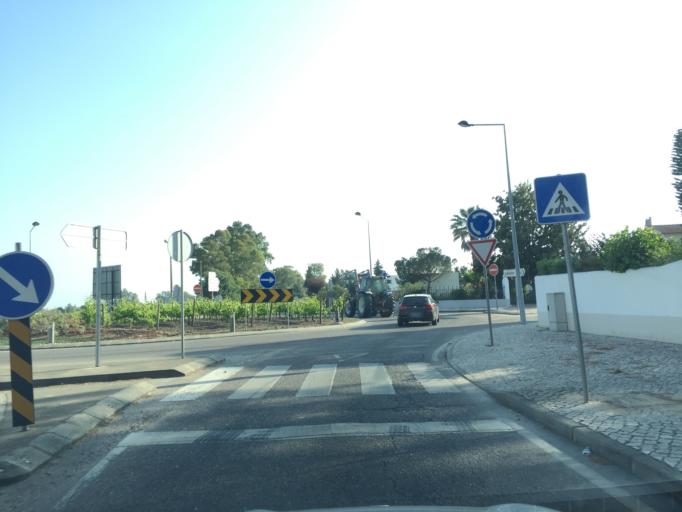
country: PT
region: Santarem
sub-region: Almeirim
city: Almeirim
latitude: 39.2046
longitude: -8.6352
